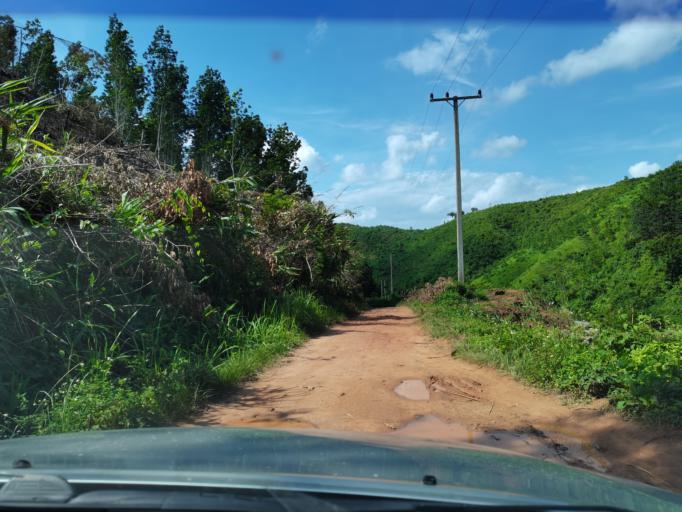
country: LA
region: Loungnamtha
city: Muang Nale
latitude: 20.5656
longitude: 101.0571
